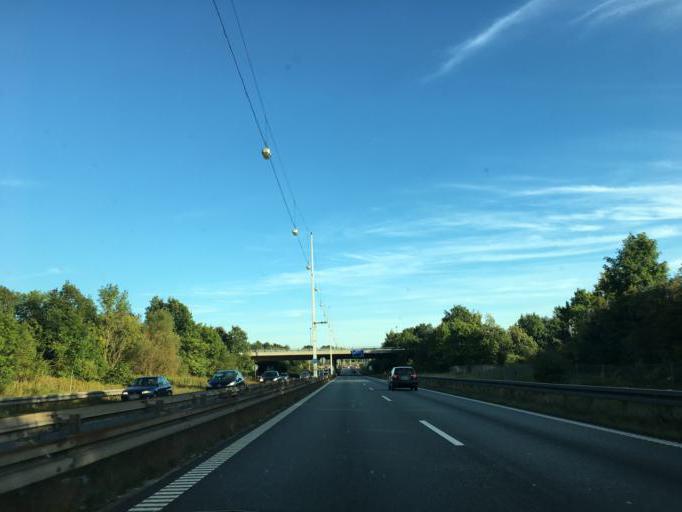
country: DK
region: Capital Region
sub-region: Kobenhavn
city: Vanlose
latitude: 55.7198
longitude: 12.4953
